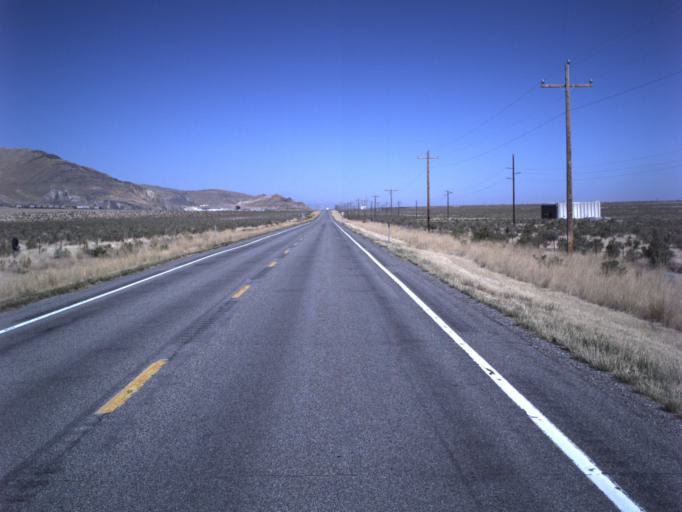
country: US
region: Utah
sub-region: Tooele County
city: Grantsville
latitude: 40.6619
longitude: -112.5402
